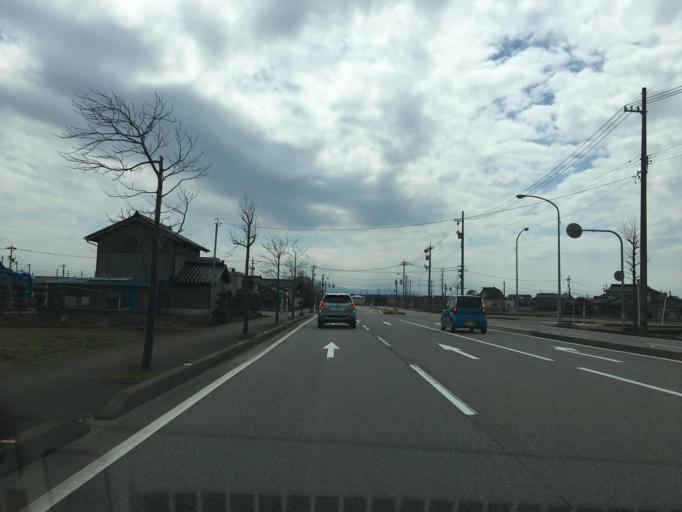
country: JP
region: Toyama
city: Kuragaki-kosugi
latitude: 36.7245
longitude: 137.1212
